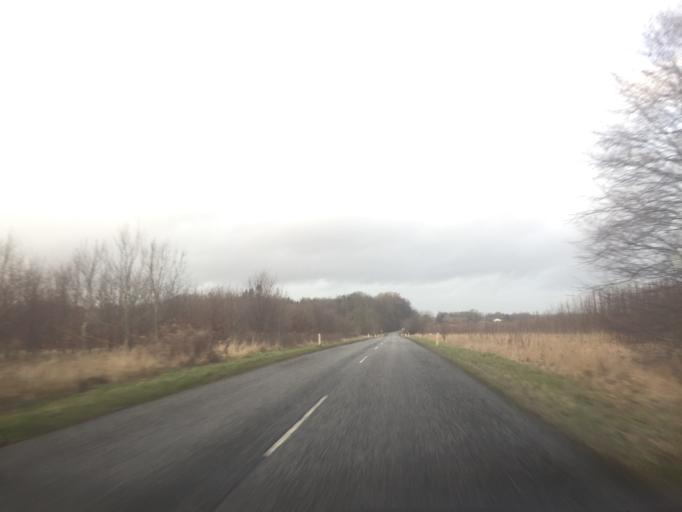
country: DK
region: Capital Region
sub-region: Egedal Kommune
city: Smorumnedre
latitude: 55.6957
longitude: 12.3229
